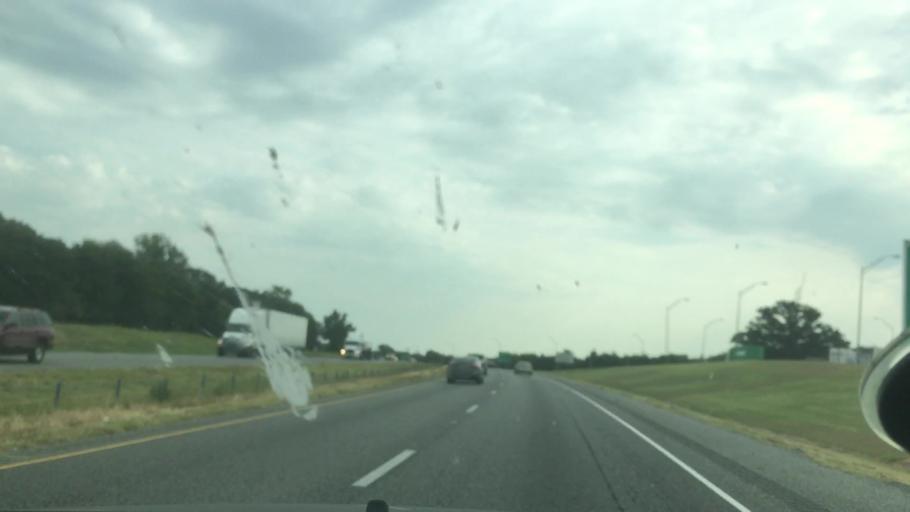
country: US
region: Oklahoma
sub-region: Bryan County
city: Colbert
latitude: 33.8429
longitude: -96.5147
